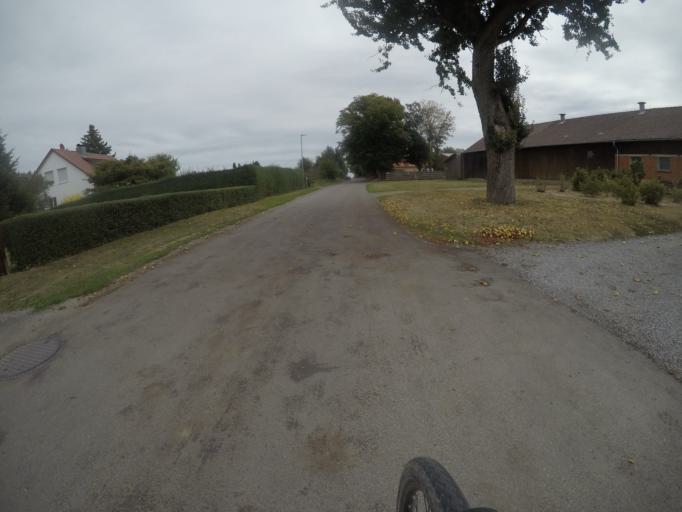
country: DE
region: Baden-Wuerttemberg
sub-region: Regierungsbezirk Stuttgart
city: Vaihingen an der Enz
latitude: 48.9502
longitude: 8.9798
